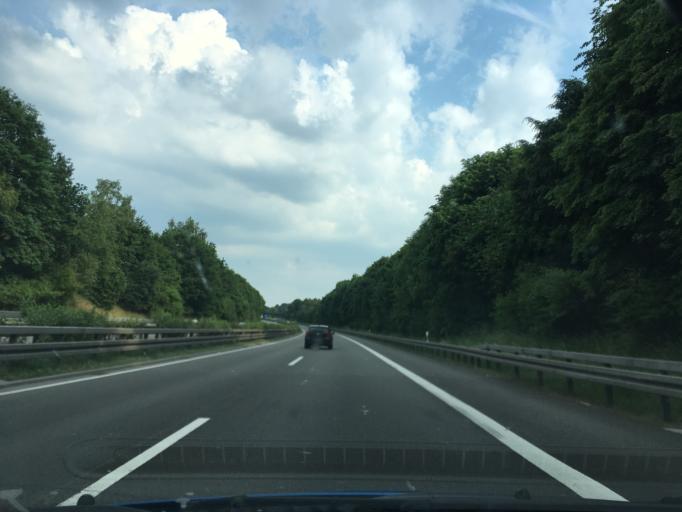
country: DE
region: Lower Saxony
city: Stelle
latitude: 53.3582
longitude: 10.1169
